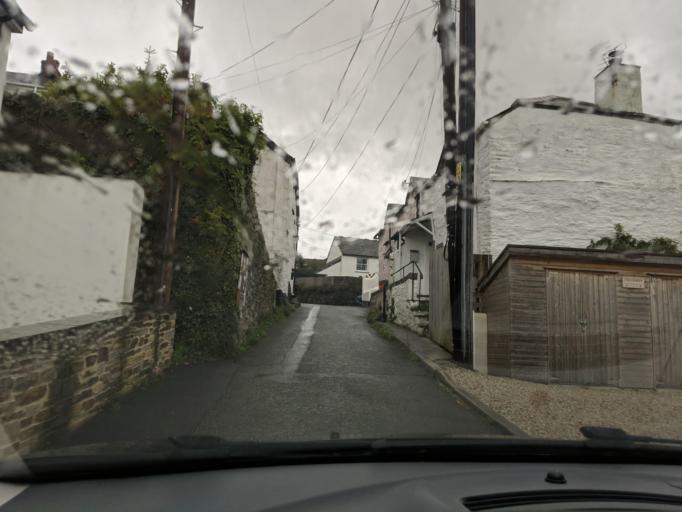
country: GB
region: England
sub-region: Cornwall
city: Wadebridge
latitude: 50.5137
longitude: -4.8212
